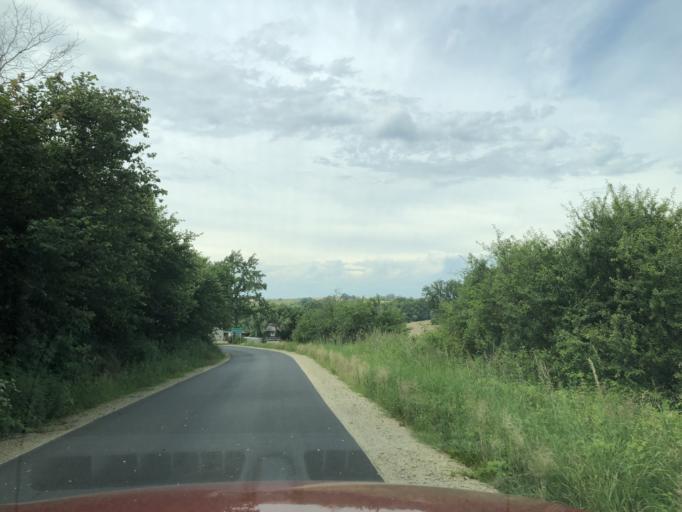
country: PL
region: Lower Silesian Voivodeship
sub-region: Powiat trzebnicki
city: Trzebnica
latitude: 51.3224
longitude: 17.0074
